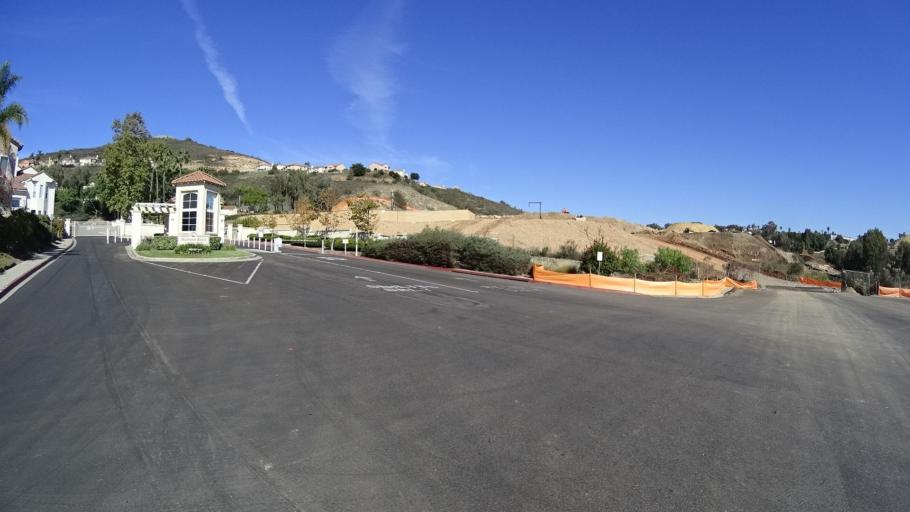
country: US
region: California
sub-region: San Diego County
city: La Presa
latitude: 32.7233
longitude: -116.9732
